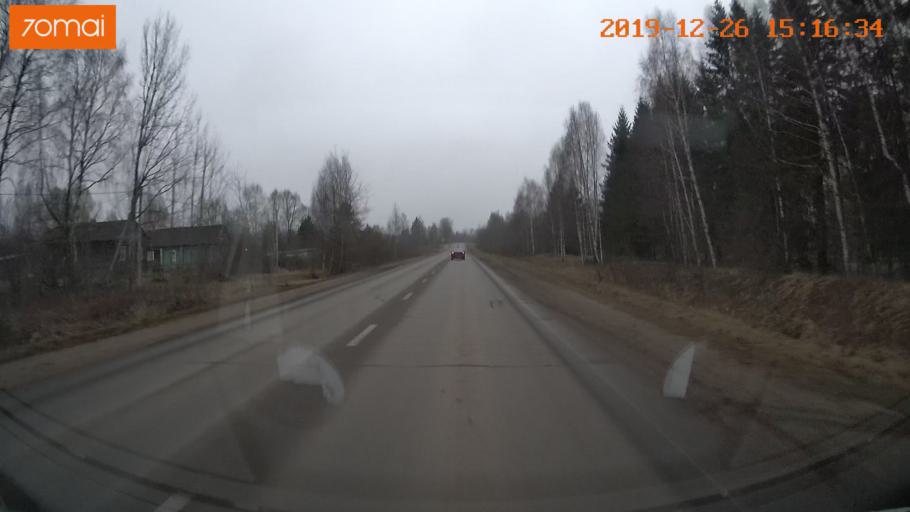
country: RU
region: Jaroslavl
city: Rybinsk
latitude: 58.0851
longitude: 38.8636
